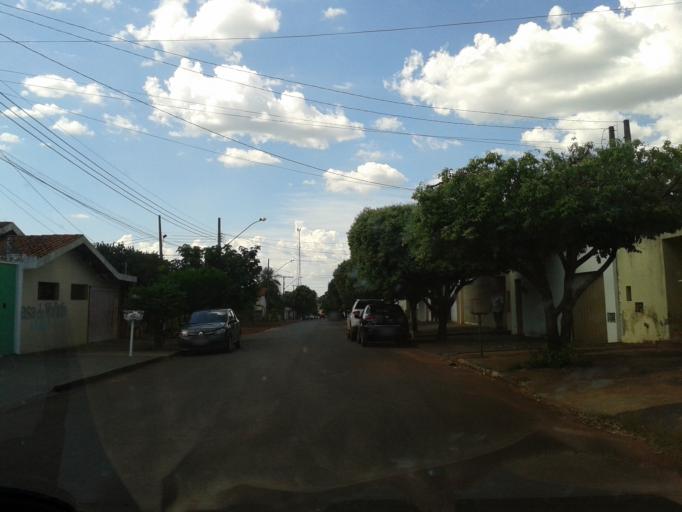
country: BR
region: Minas Gerais
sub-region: Ituiutaba
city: Ituiutaba
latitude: -18.9896
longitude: -49.4686
